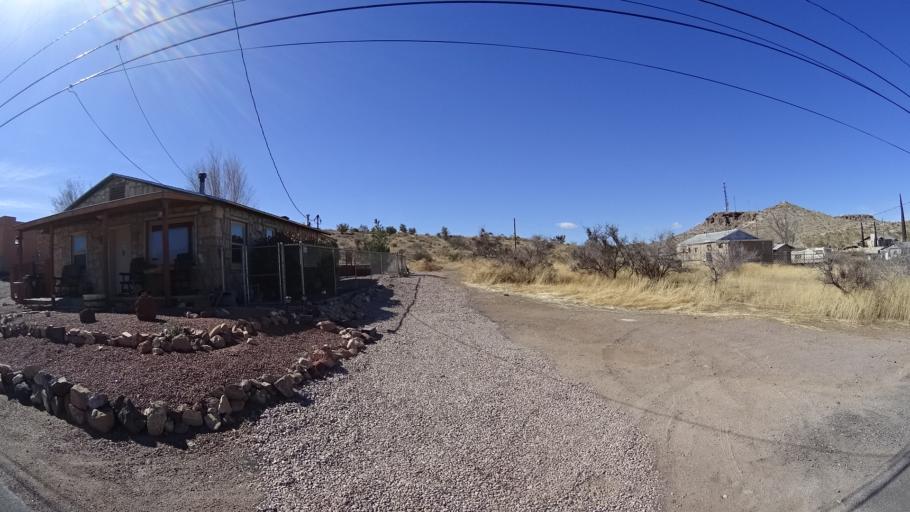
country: US
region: Arizona
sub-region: Mohave County
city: Kingman
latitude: 35.1935
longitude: -114.0352
